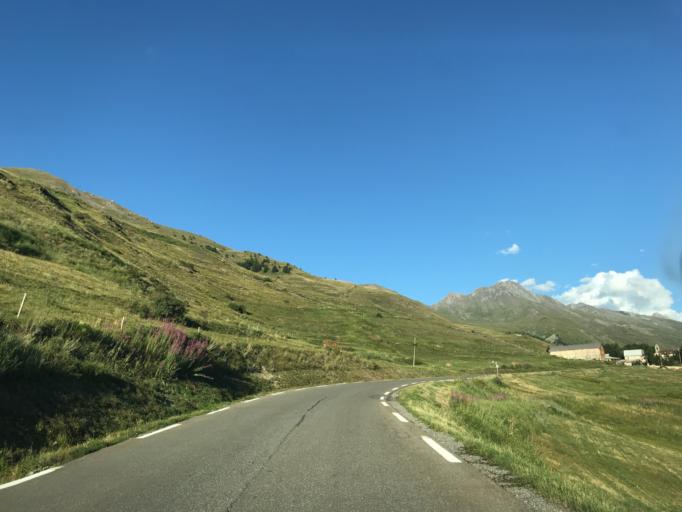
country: IT
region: Piedmont
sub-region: Provincia di Cuneo
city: Pontechianale
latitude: 44.7246
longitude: 6.8786
